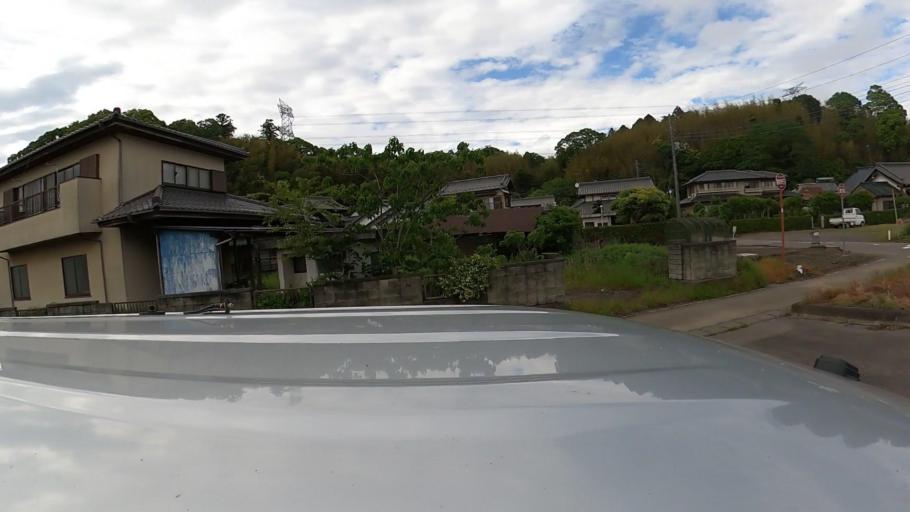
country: JP
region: Ibaraki
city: Ryugasaki
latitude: 35.9584
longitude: 140.2104
